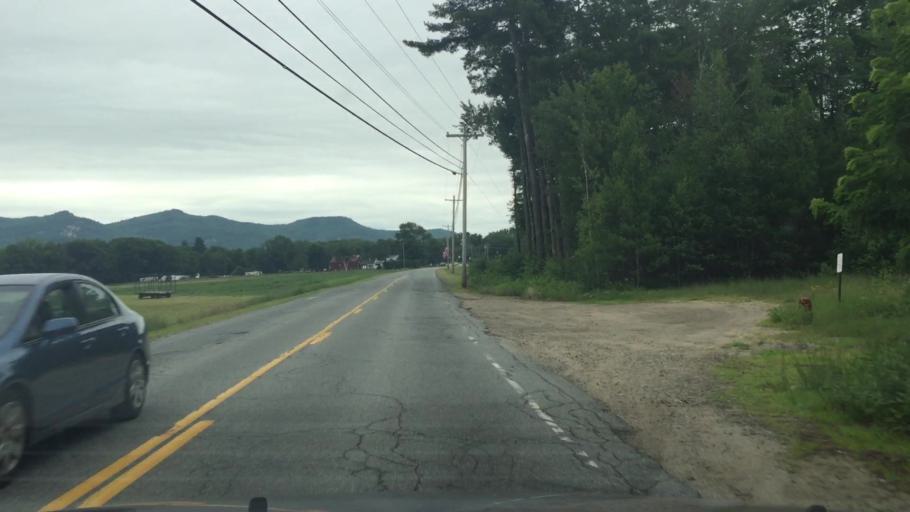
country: US
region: New Hampshire
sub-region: Carroll County
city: North Conway
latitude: 44.0614
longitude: -71.1533
